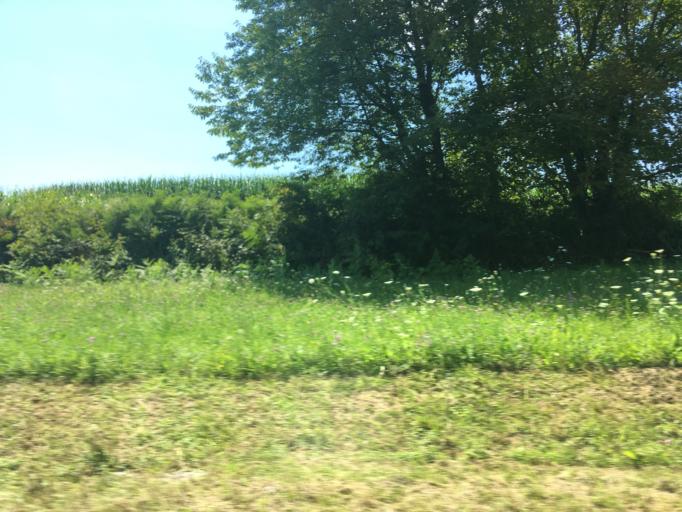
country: SI
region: Metlika
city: Metlika
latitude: 45.6011
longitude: 15.3367
